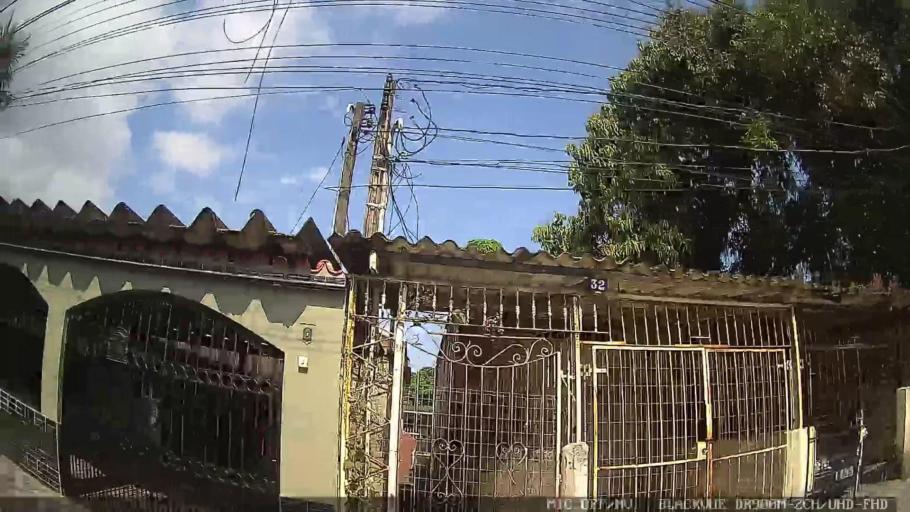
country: BR
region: Sao Paulo
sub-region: Santos
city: Santos
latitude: -23.9450
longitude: -46.3051
